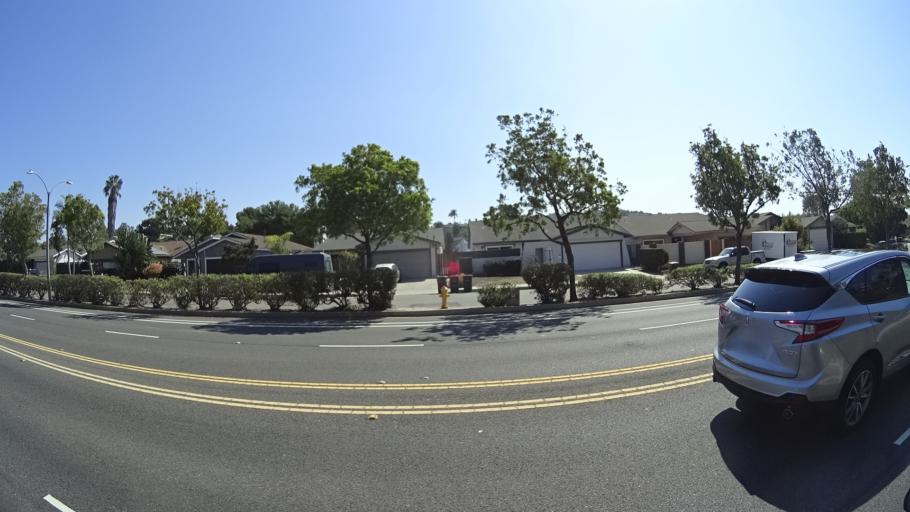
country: US
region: California
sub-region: Orange County
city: San Juan Capistrano
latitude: 33.4615
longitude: -117.6428
